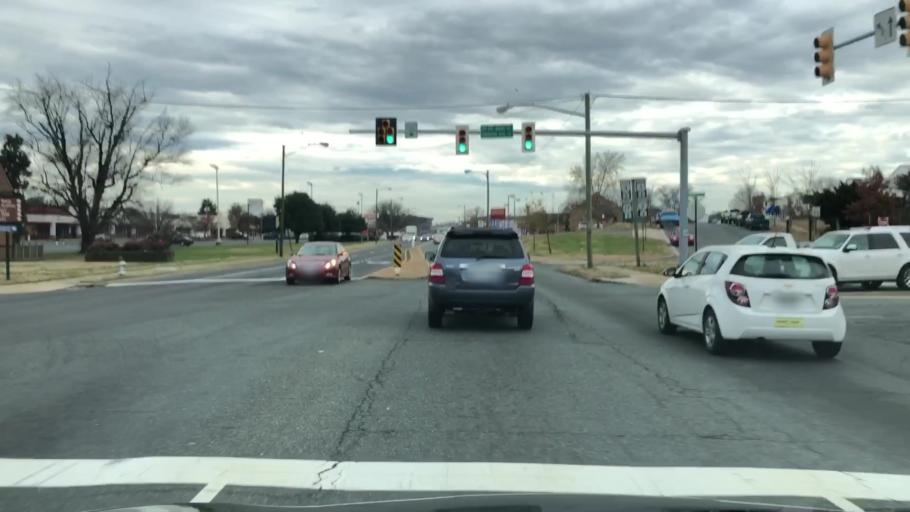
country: US
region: Virginia
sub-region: Stafford County
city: Falmouth
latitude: 38.3183
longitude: -77.4722
